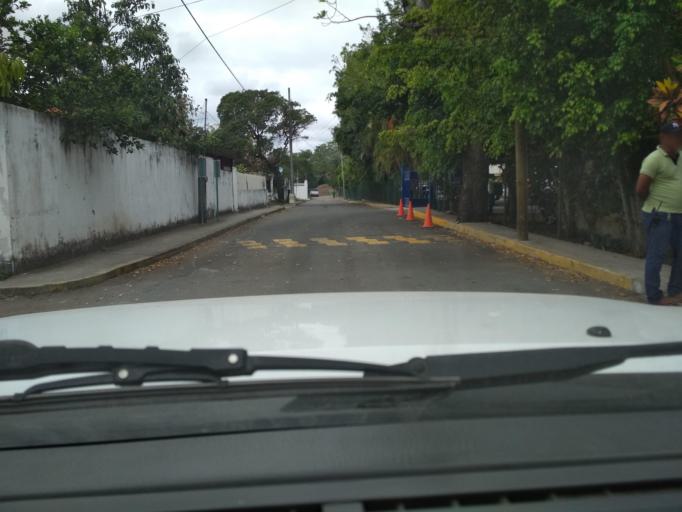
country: MX
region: Veracruz
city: Paso del Toro
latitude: 19.0556
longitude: -96.1361
